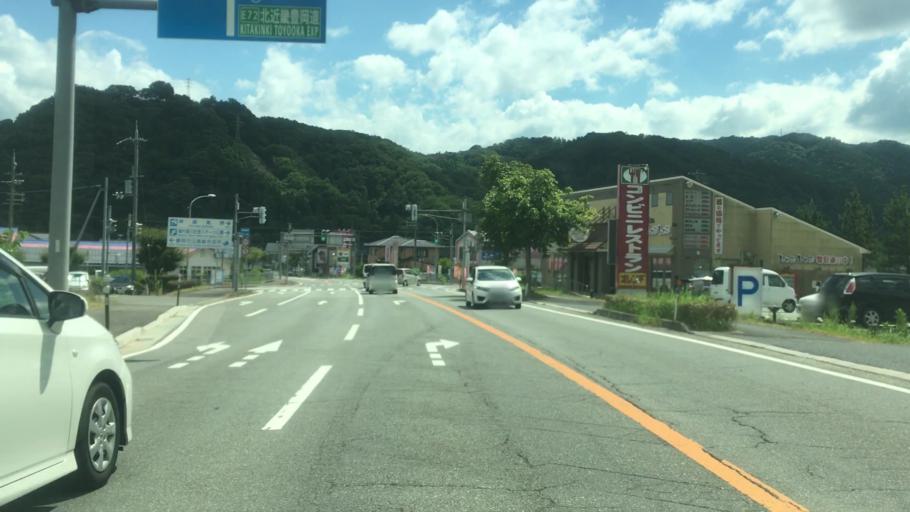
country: JP
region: Hyogo
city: Toyooka
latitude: 35.4702
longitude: 134.7688
